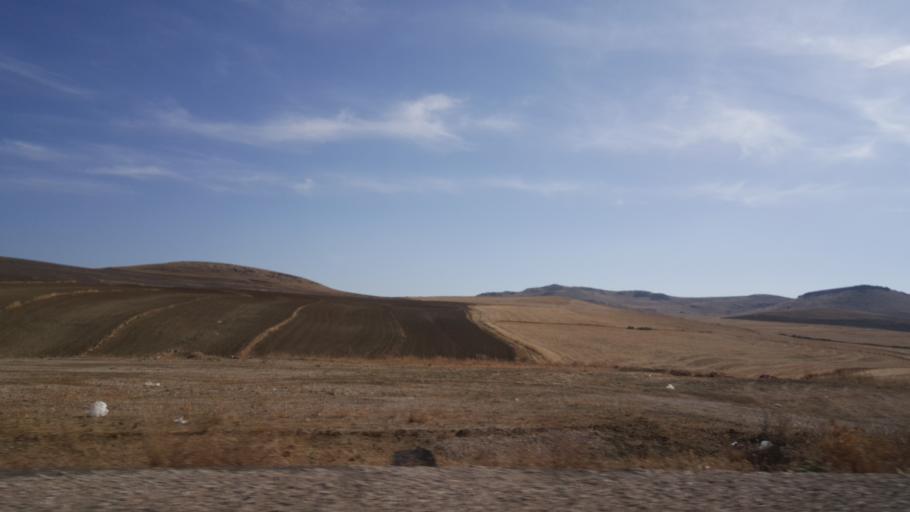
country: TR
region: Ankara
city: Yenice
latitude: 39.3656
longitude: 32.7120
